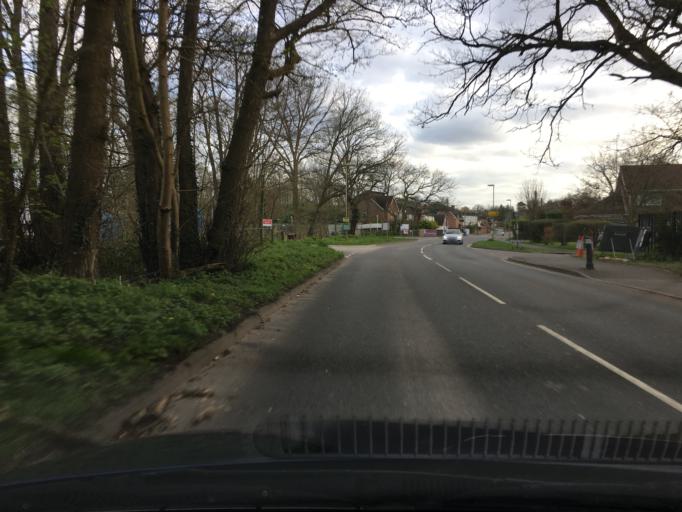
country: GB
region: England
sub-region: Hampshire
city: Yateley
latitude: 51.3428
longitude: -0.8160
